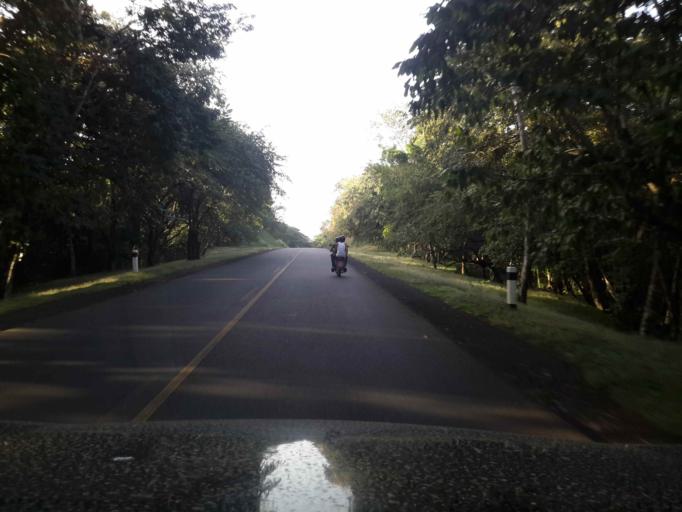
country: NI
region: Rio San Juan
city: San Miguelito
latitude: 11.4077
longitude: -84.8342
